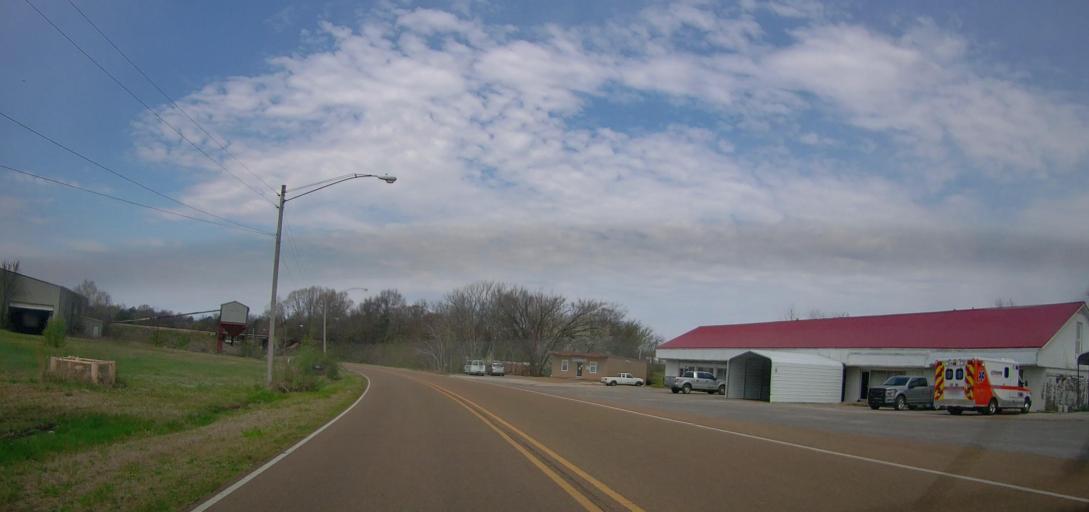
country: US
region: Mississippi
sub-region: Marshall County
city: Holly Springs
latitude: 34.7647
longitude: -89.4317
